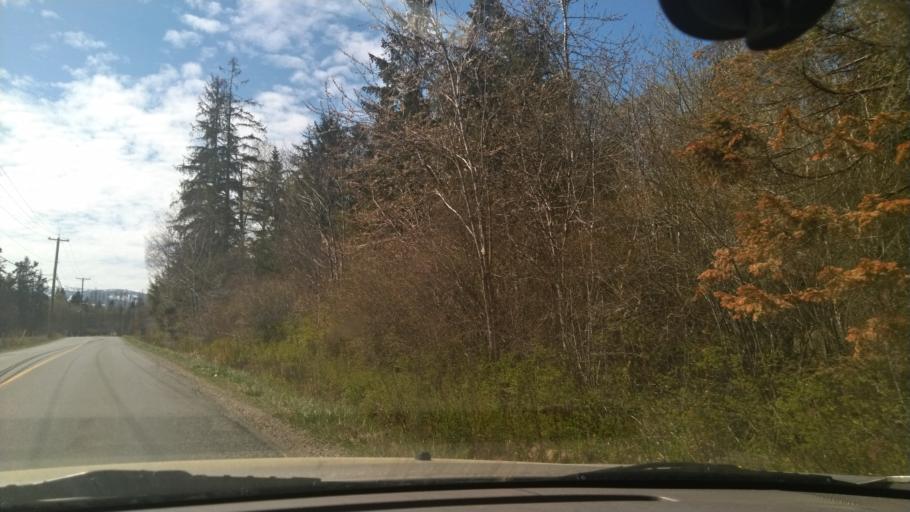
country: CA
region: British Columbia
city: Courtenay
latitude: 49.6960
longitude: -125.0084
